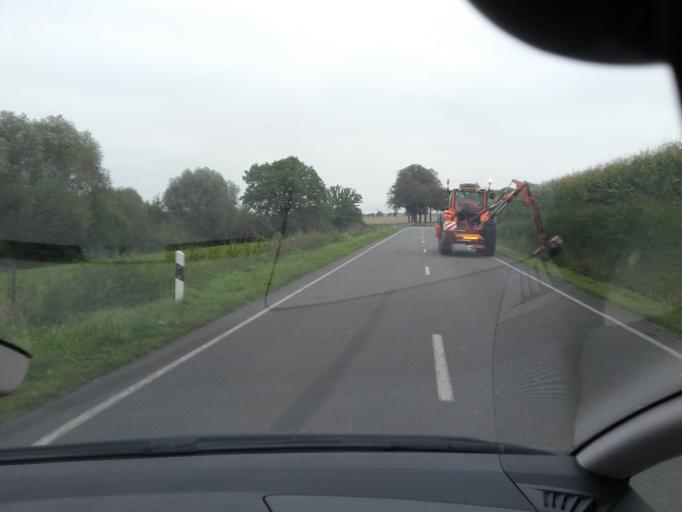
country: LU
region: Diekirch
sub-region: Canton de Redange
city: Ell
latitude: 49.7315
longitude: 5.8480
